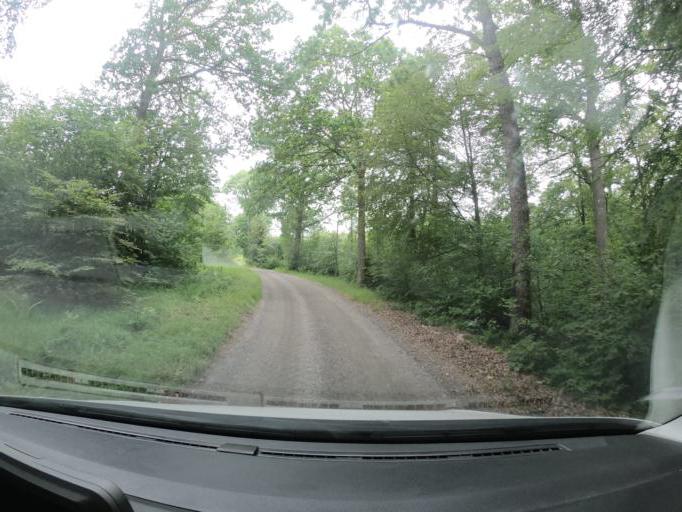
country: SE
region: Skane
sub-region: Hassleholms Kommun
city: Sosdala
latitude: 56.1012
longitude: 13.5491
